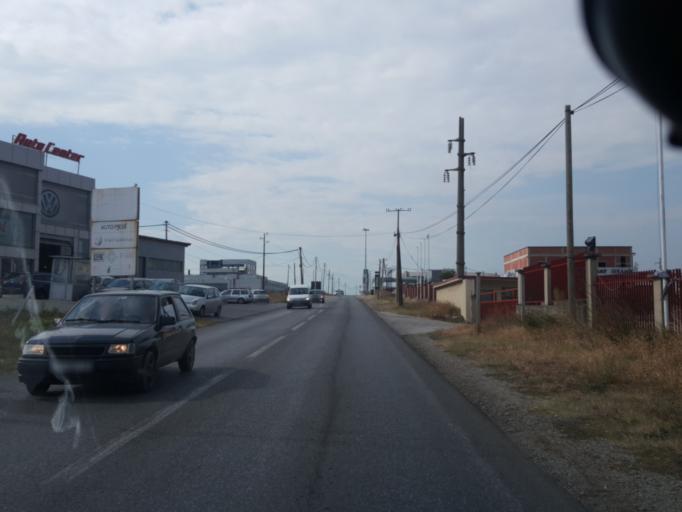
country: XK
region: Gjakova
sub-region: Komuna e Gjakoves
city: Gjakove
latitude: 42.3676
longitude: 20.4628
